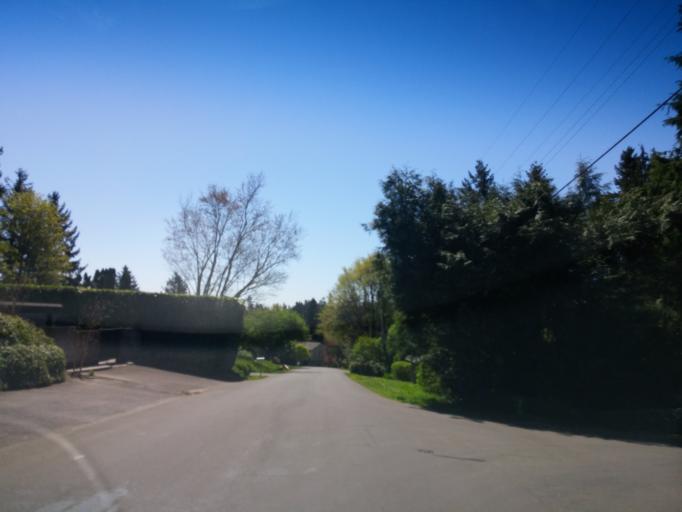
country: US
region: Oregon
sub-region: Washington County
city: West Haven
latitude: 45.5206
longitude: -122.7806
